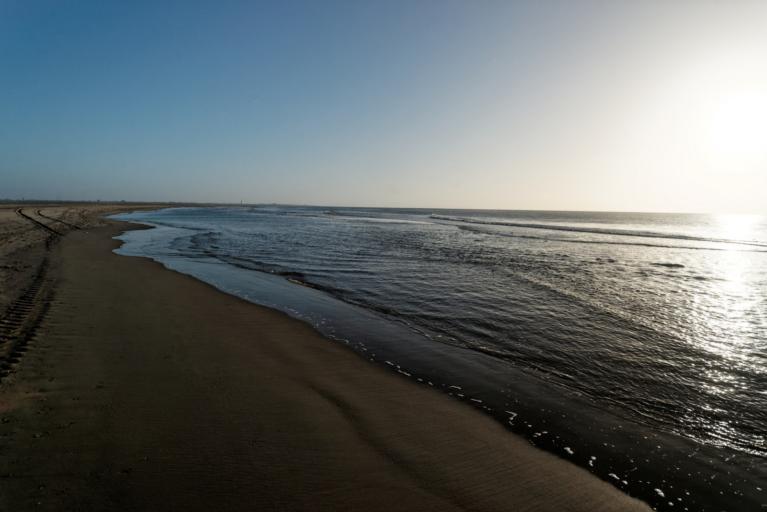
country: NL
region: North Holland
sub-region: Gemeente Den Helder
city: Den Helder
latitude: 53.0178
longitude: 4.7085
